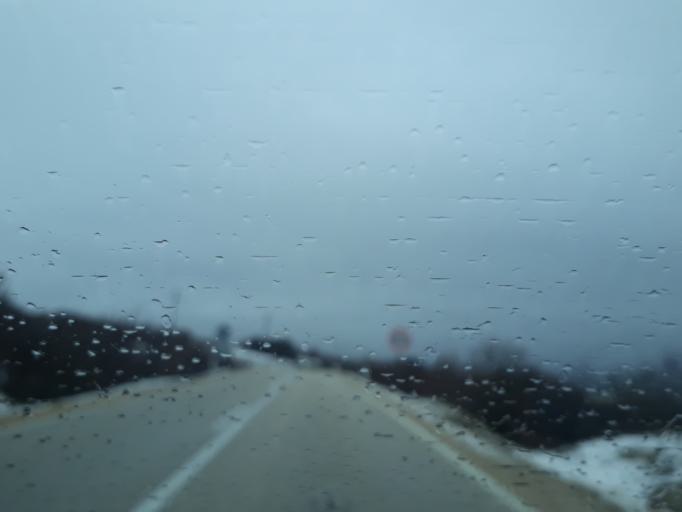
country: BA
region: Federation of Bosnia and Herzegovina
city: Tomislavgrad
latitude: 43.7883
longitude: 17.2220
